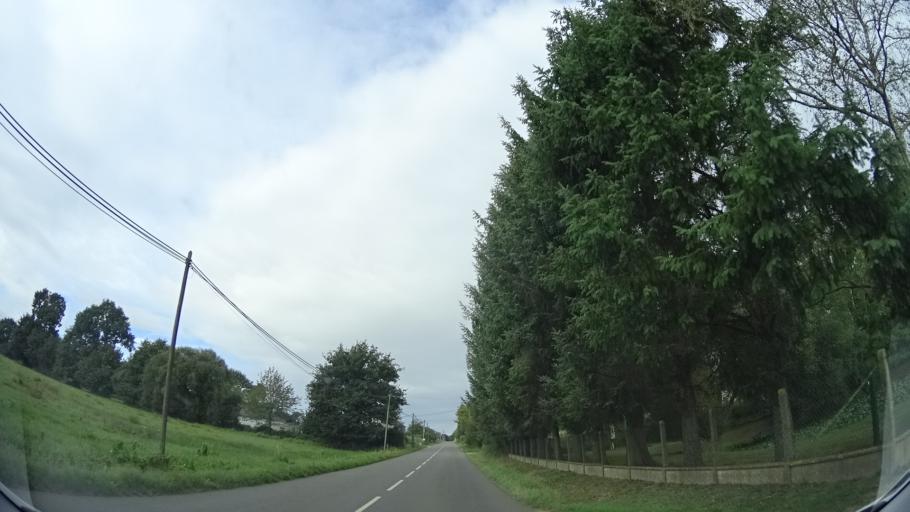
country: FR
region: Brittany
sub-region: Departement d'Ille-et-Vilaine
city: Hede-Bazouges
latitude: 48.2980
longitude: -1.7724
